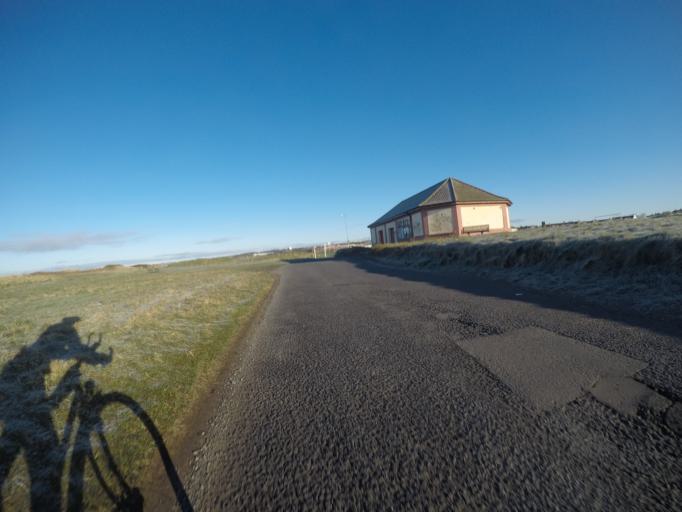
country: GB
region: Scotland
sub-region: North Ayrshire
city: Stevenston
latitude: 55.6298
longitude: -4.7508
